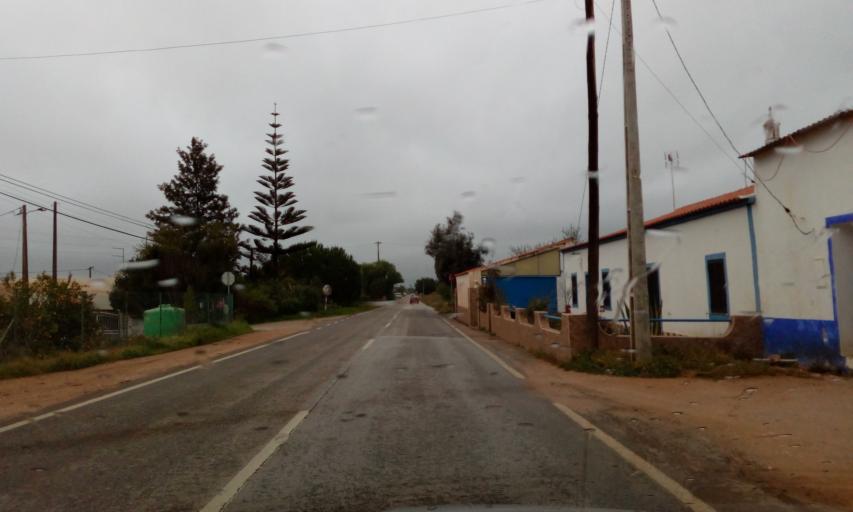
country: PT
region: Faro
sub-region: Albufeira
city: Guia
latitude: 37.1717
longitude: -8.3405
